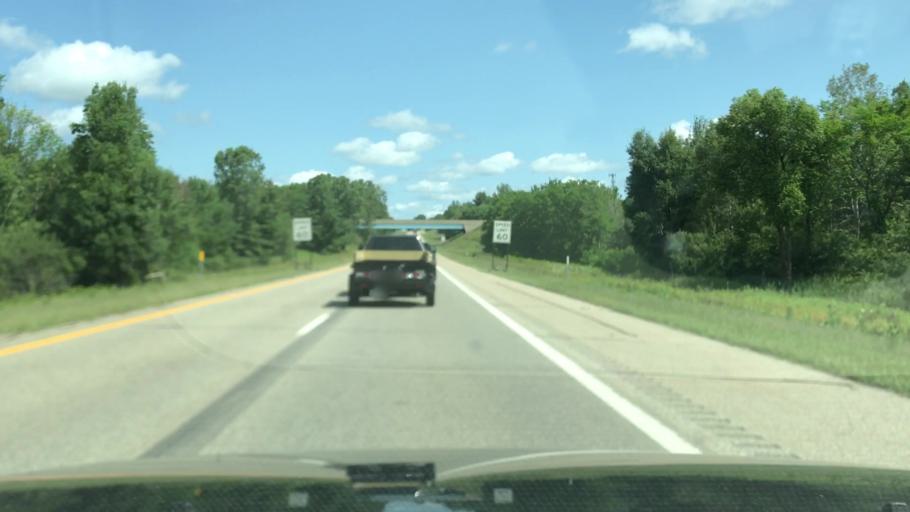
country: US
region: Michigan
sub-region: Mecosta County
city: Big Rapids
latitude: 43.7401
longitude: -85.5312
